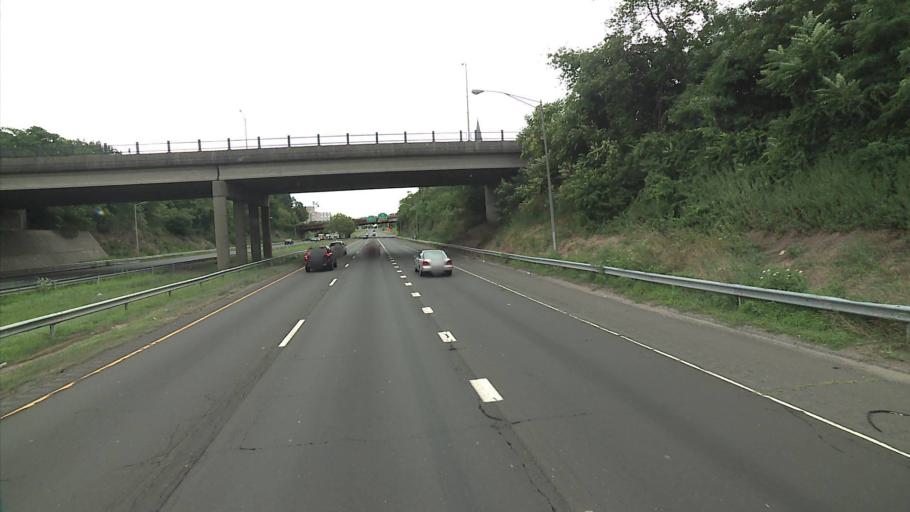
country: US
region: Connecticut
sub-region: Fairfield County
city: Bridgeport
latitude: 41.1822
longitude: -73.1941
